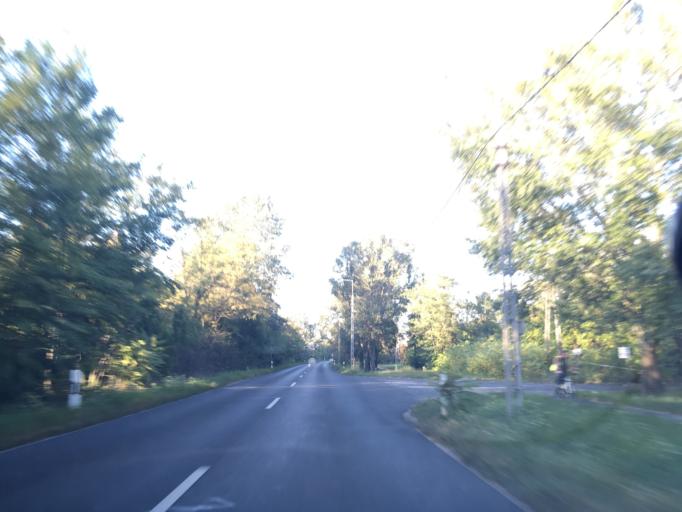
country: HU
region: Pest
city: Szazhalombatta
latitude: 47.3052
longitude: 18.8954
